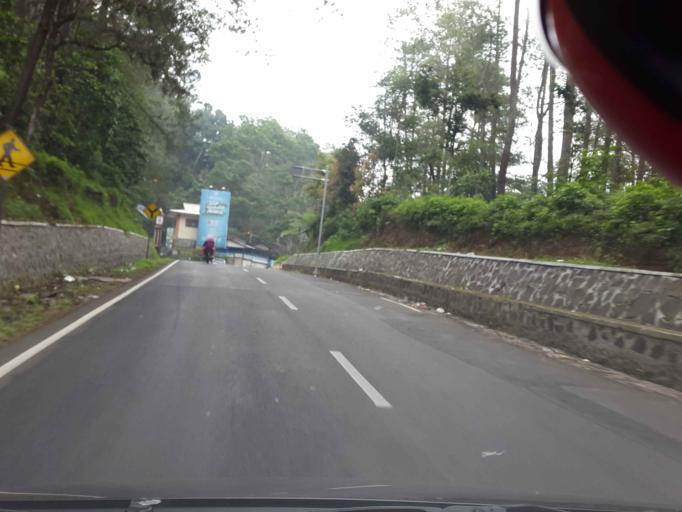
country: ID
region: West Java
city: Lembang
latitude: -6.7749
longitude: 107.6373
